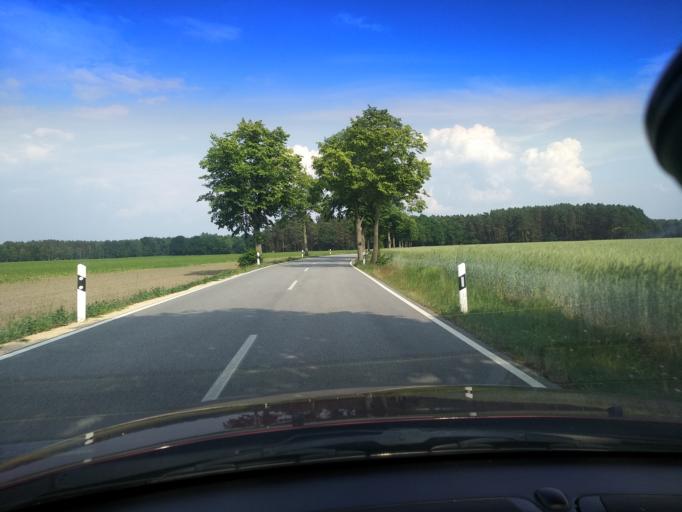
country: DE
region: Saxony
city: Klitten
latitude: 51.3475
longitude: 14.6173
